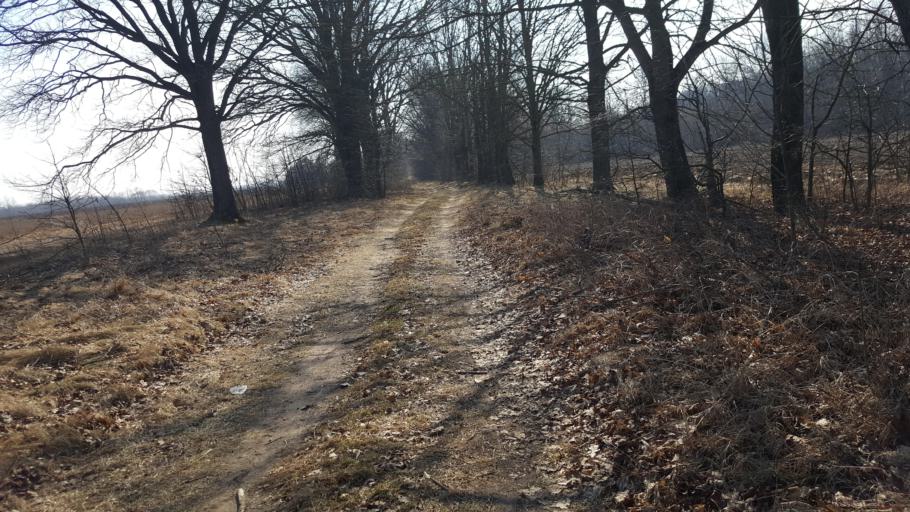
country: BY
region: Brest
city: Zhabinka
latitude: 52.3176
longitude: 23.9304
